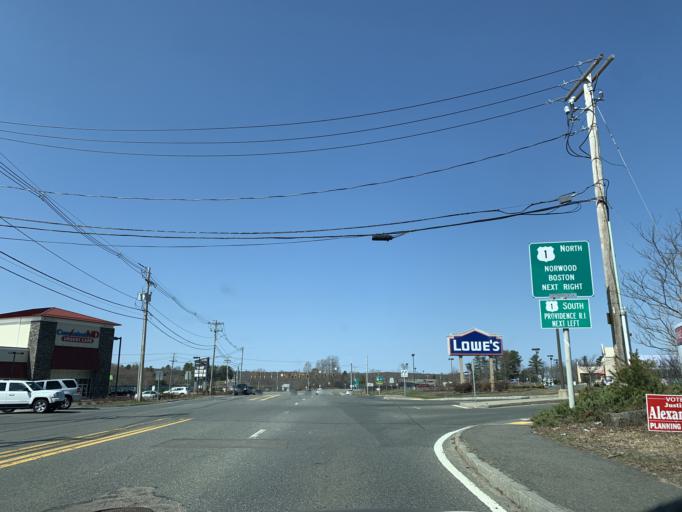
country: US
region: Massachusetts
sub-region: Norfolk County
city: Plainville
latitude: 42.0275
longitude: -71.3099
